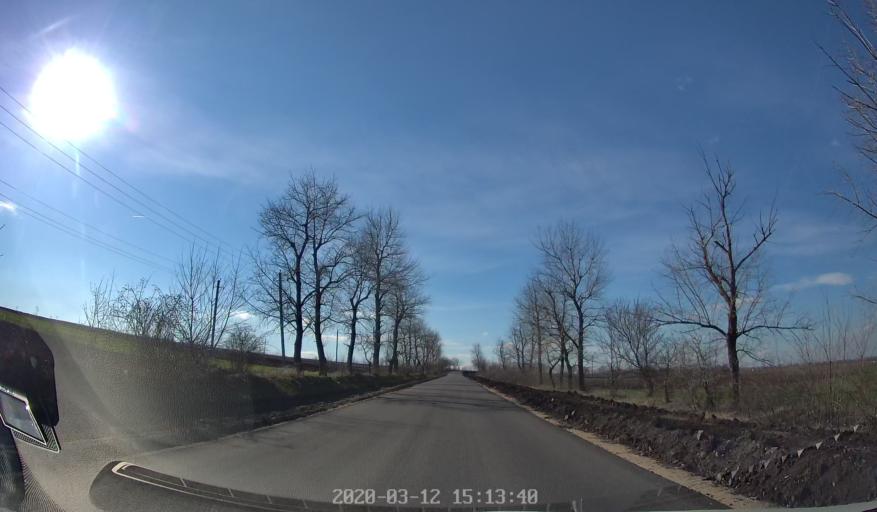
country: MD
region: Chisinau
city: Ciorescu
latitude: 47.2307
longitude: 28.9606
